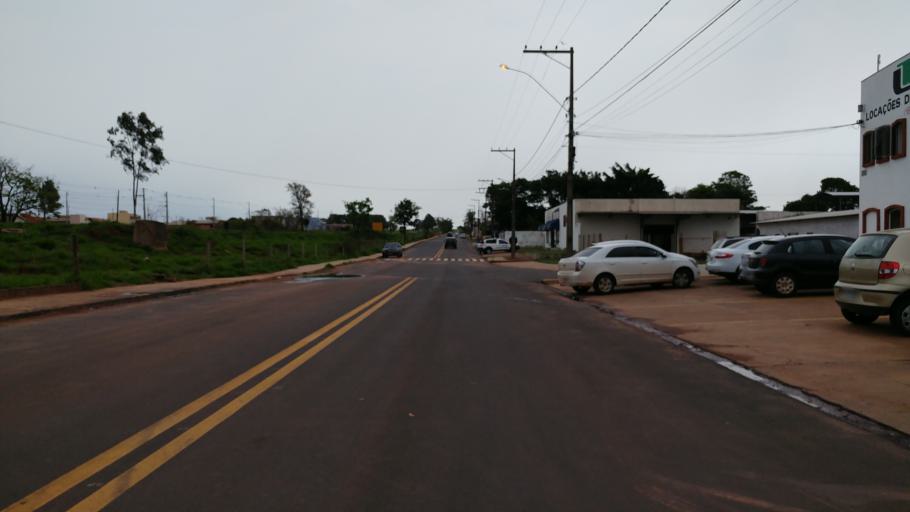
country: BR
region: Sao Paulo
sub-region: Paraguacu Paulista
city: Paraguacu Paulista
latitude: -22.4421
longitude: -50.5841
